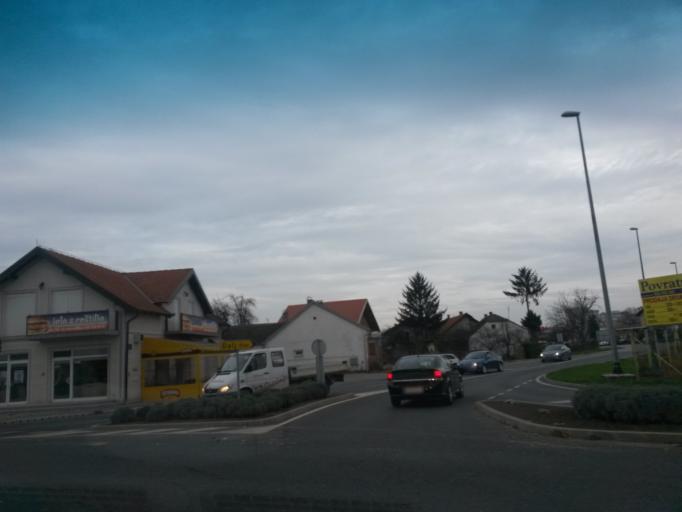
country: HR
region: Vukovarsko-Srijemska
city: Borovo
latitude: 45.3732
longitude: 18.9505
